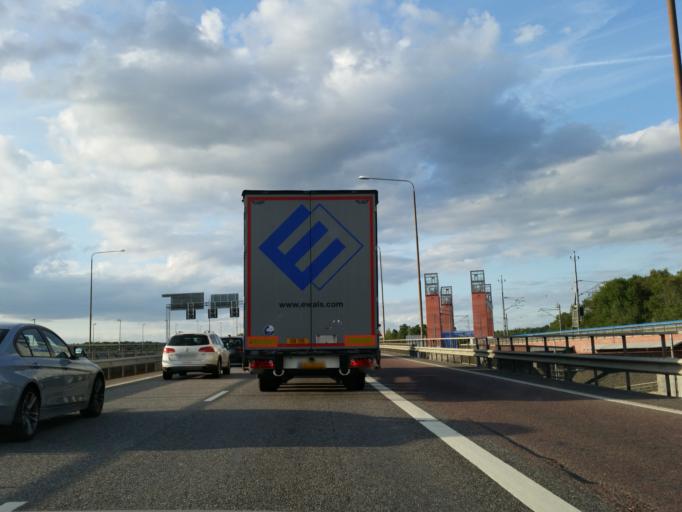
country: SE
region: Stockholm
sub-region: Sodertalje Kommun
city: Soedertaelje
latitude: 59.1819
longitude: 17.6421
